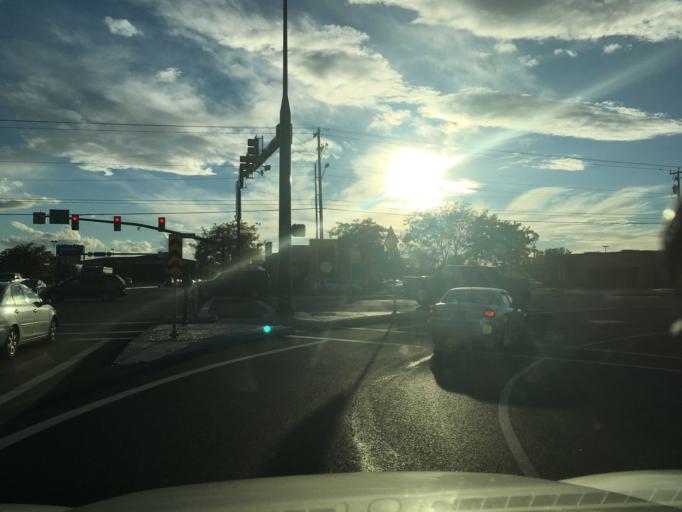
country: US
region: Utah
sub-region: Davis County
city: Layton
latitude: 41.0731
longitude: -111.9786
